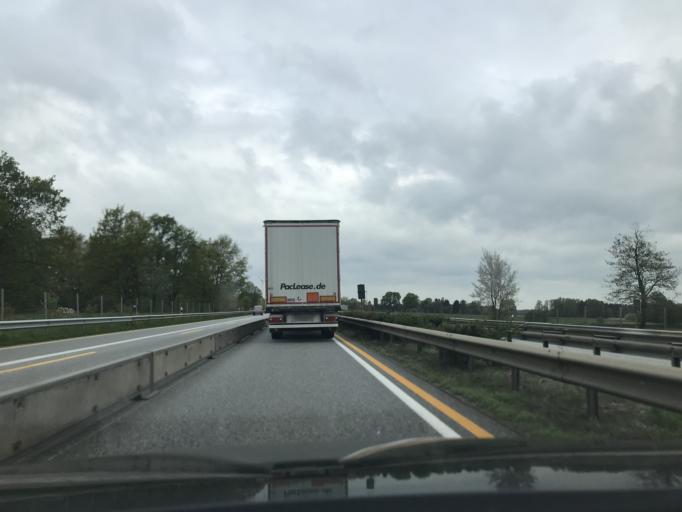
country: DE
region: Lower Saxony
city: Langwedel
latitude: 52.9912
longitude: 9.1988
